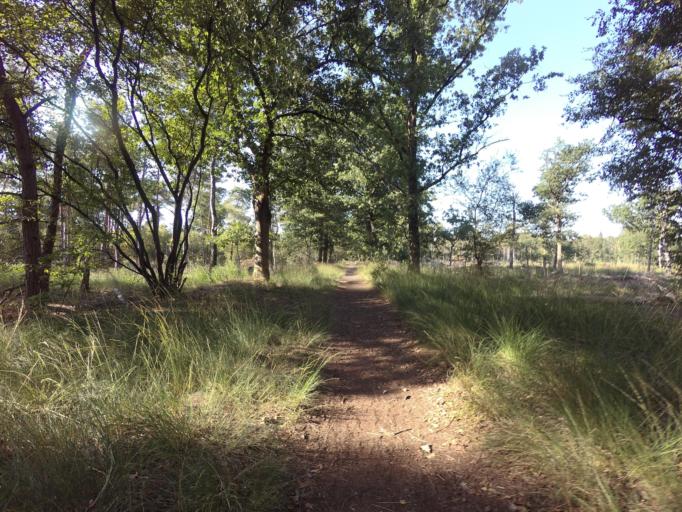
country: NL
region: North Brabant
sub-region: Gemeente Someren
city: Someren
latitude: 51.3756
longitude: 5.6562
